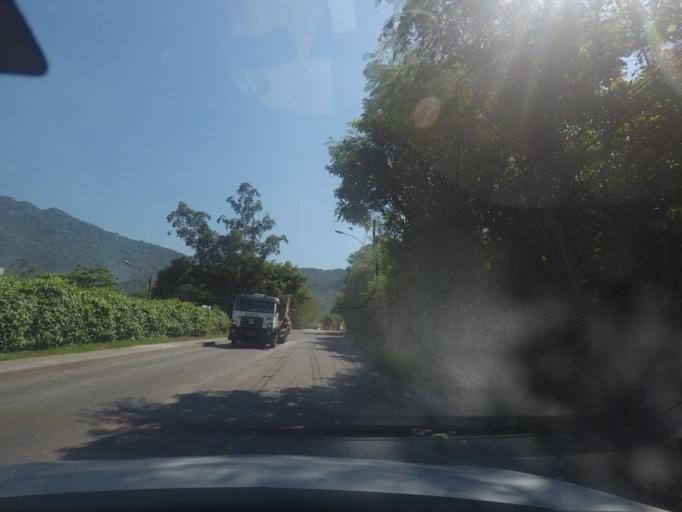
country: BR
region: Rio de Janeiro
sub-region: Nilopolis
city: Nilopolis
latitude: -22.9854
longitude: -43.4521
